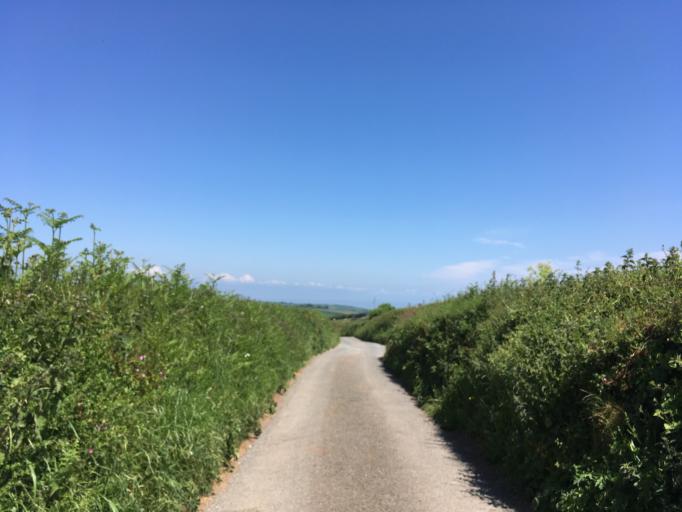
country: GB
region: England
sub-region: Devon
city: Dartmouth
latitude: 50.3487
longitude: -3.5413
